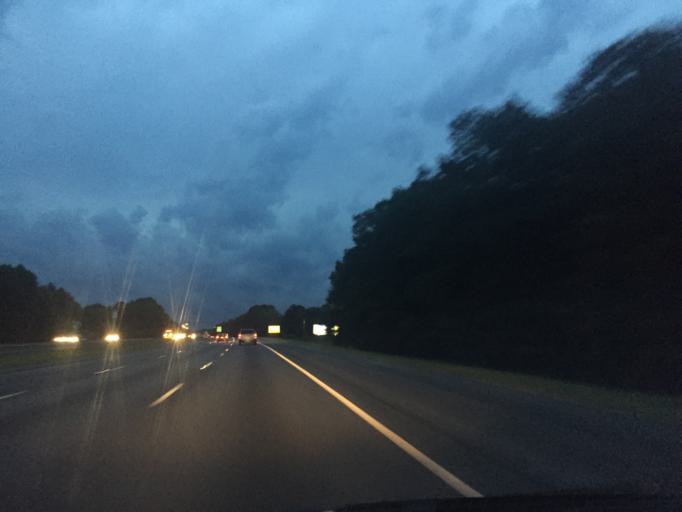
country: US
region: Georgia
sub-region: Bryan County
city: Richmond Hill
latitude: 31.9921
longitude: -81.2954
